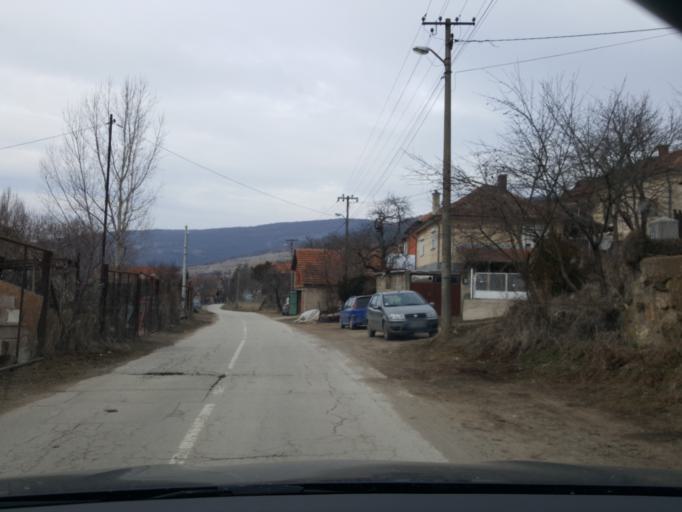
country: RS
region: Central Serbia
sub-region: Pirotski Okrug
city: Dimitrovgrad
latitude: 43.0067
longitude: 22.7598
